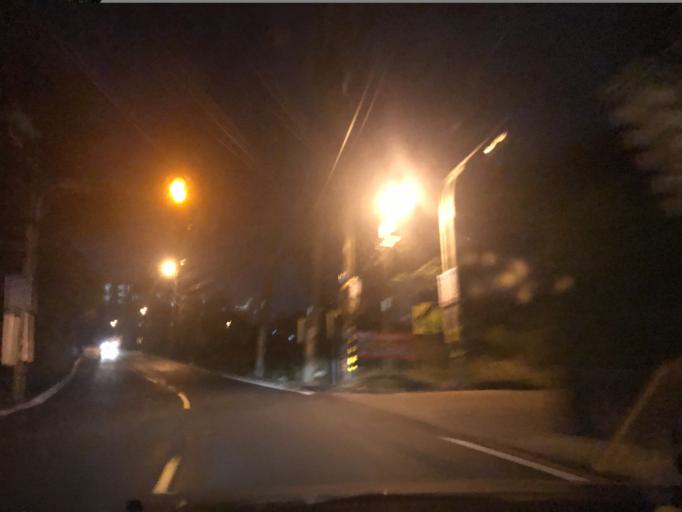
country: TW
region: Taiwan
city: Taoyuan City
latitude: 24.9436
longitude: 121.2356
